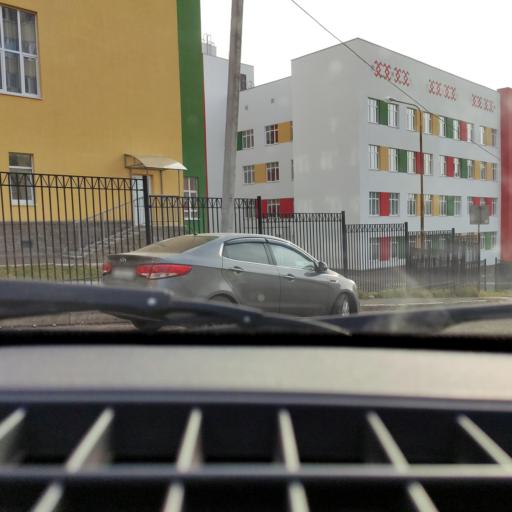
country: RU
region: Bashkortostan
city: Ufa
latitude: 54.6905
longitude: 55.9946
